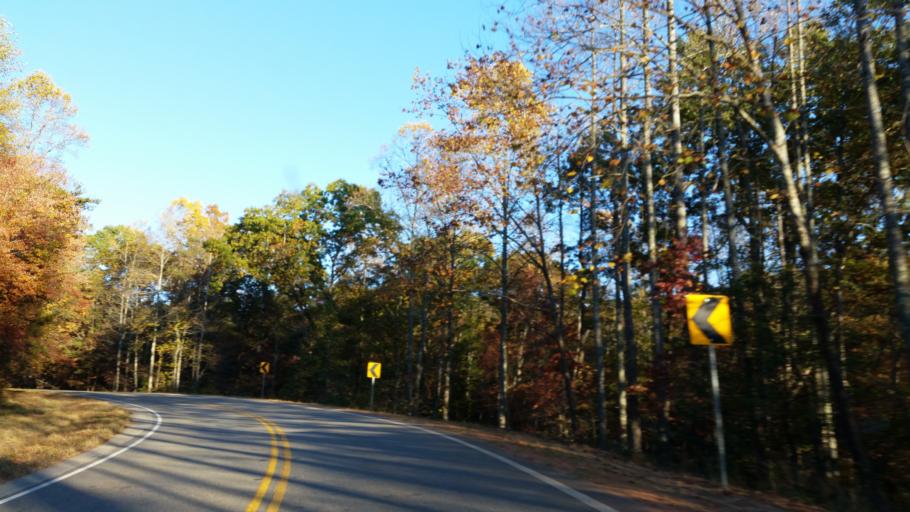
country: US
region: Georgia
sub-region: Dawson County
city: Dawsonville
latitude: 34.5502
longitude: -84.2414
